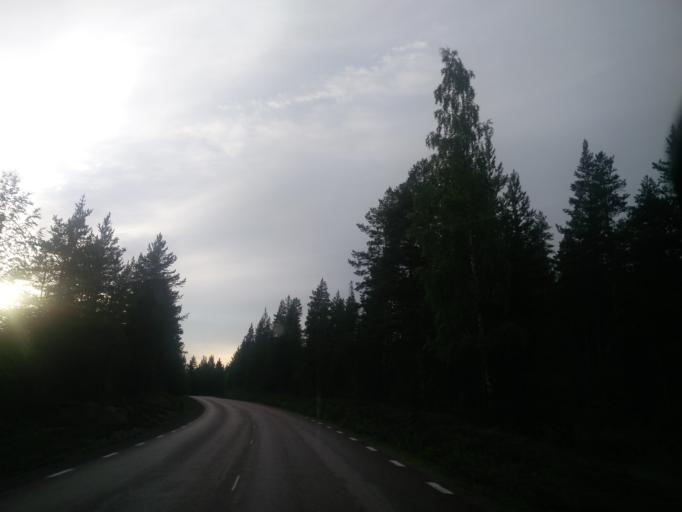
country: NO
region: Hedmark
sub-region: Trysil
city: Innbygda
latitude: 61.7849
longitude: 12.9347
